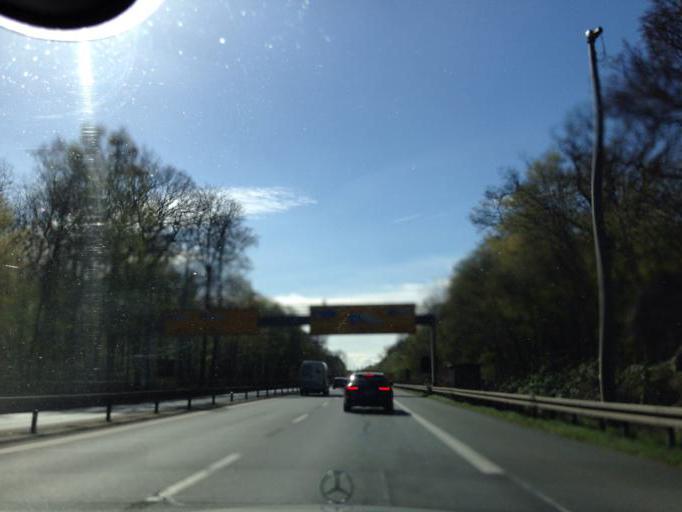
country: DE
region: Lower Saxony
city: Laatzen
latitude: 52.3445
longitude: 9.7992
